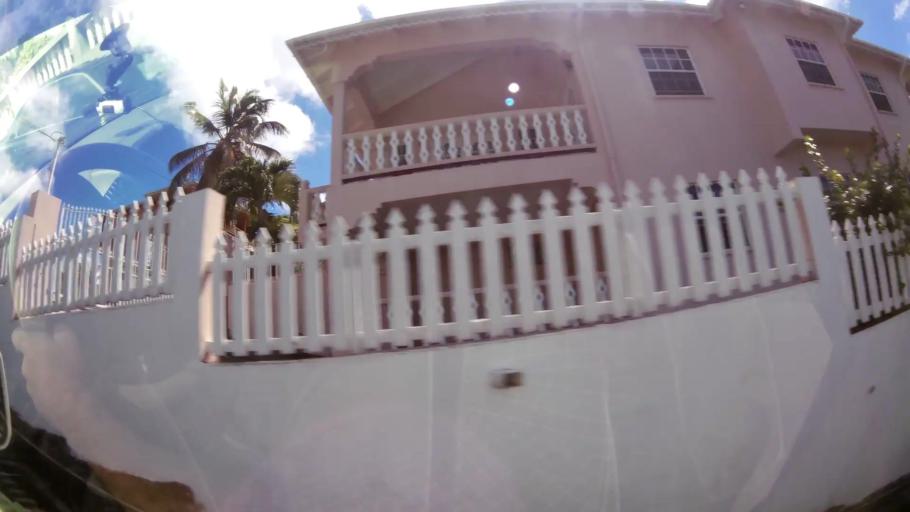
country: VC
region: Saint George
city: Kingstown
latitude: 13.1418
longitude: -61.2260
